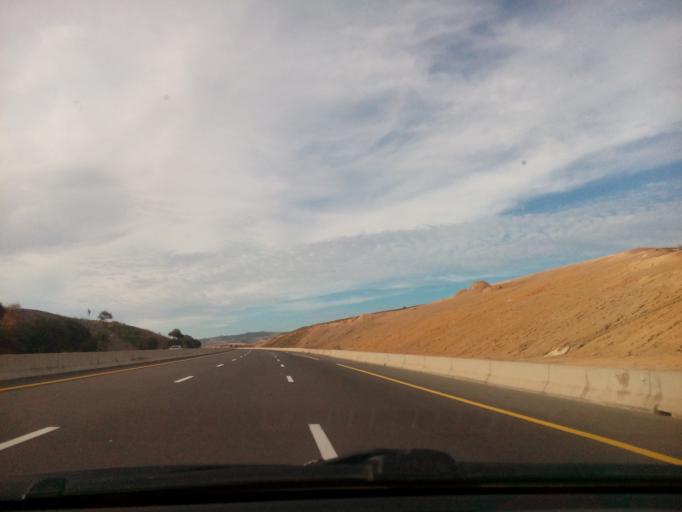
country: DZ
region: Sidi Bel Abbes
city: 'Ain el Berd
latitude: 35.4448
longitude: -0.4089
